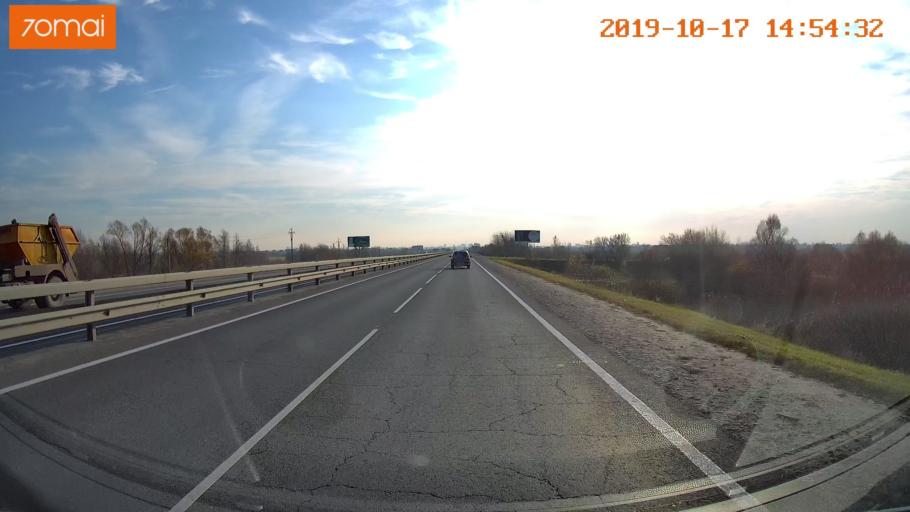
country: RU
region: Rjazan
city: Polyany
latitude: 54.6800
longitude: 39.8312
